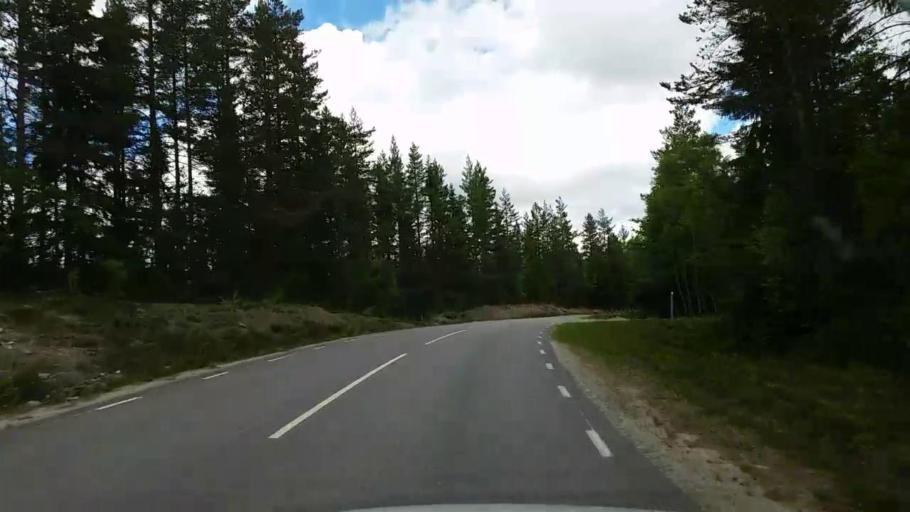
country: SE
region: Gaevleborg
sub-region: Bollnas Kommun
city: Vittsjo
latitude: 61.1153
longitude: 16.1469
